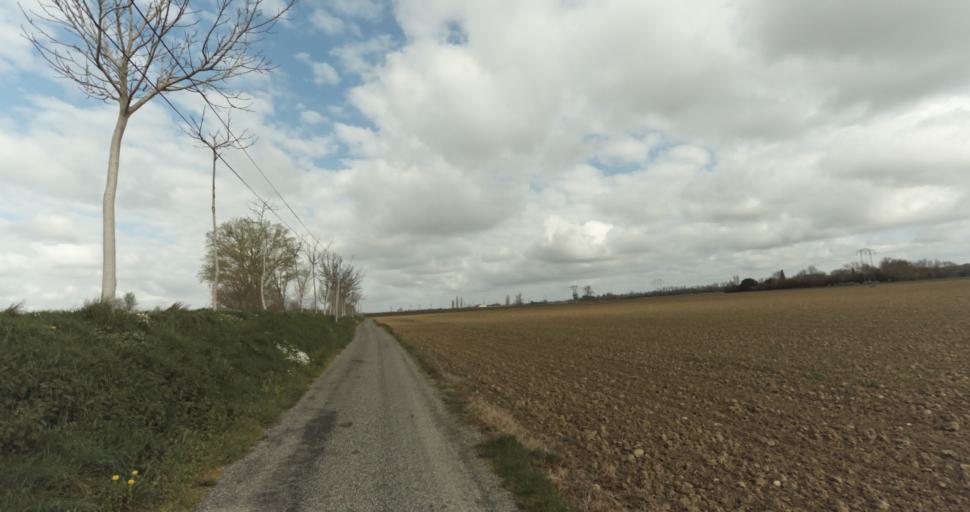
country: FR
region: Midi-Pyrenees
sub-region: Departement de la Haute-Garonne
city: Auterive
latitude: 43.3431
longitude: 1.4479
